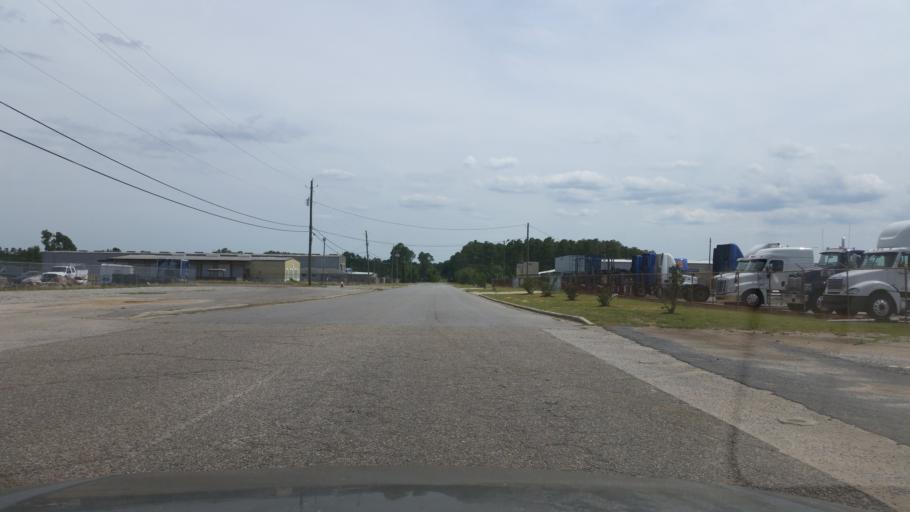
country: US
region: Florida
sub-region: Escambia County
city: Ferry Pass
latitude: 30.5246
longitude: -87.1978
